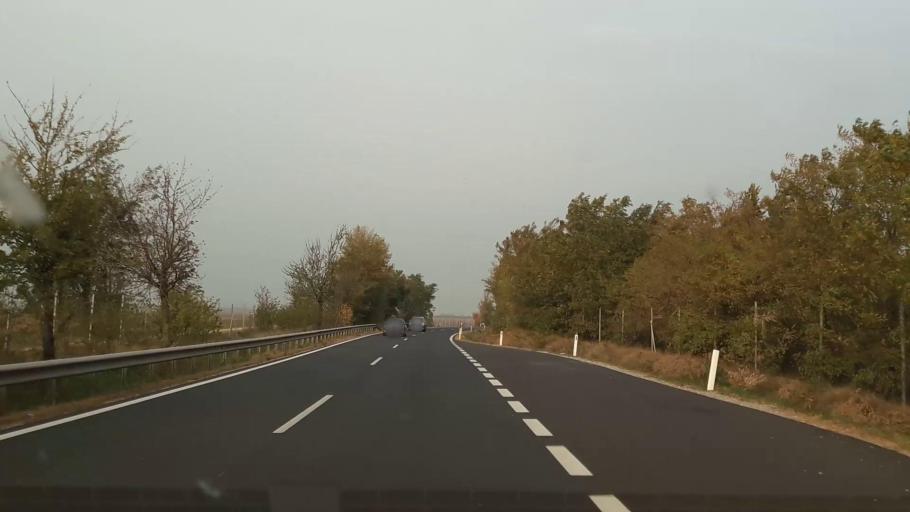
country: AT
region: Burgenland
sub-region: Politischer Bezirk Neusiedl am See
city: Gols
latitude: 47.9318
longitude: 16.9158
